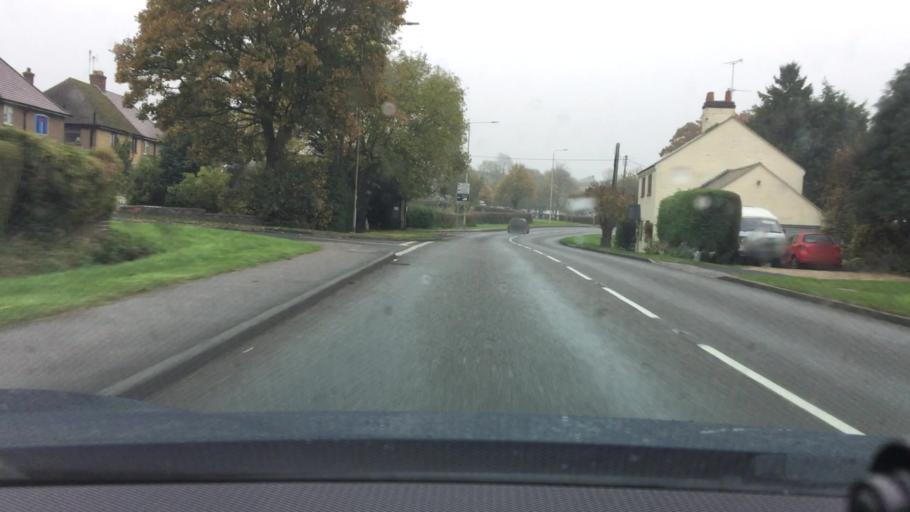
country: GB
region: England
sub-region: Leicestershire
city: Market Harborough
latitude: 52.4789
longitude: -0.9668
